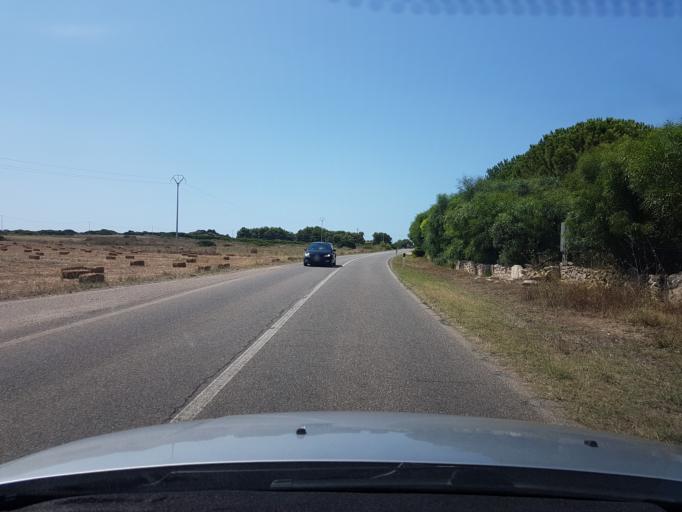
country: IT
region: Sardinia
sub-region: Provincia di Oristano
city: Riola Sardo
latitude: 40.0216
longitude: 8.4534
